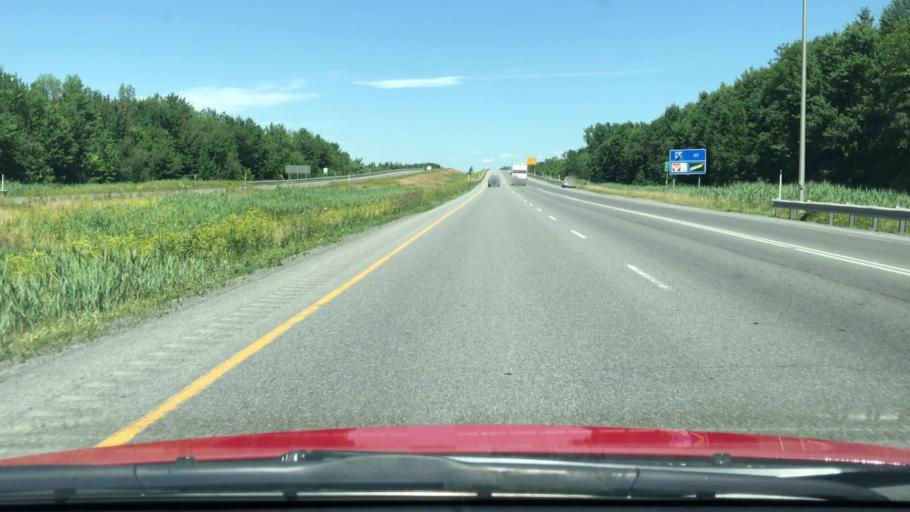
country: CA
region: Quebec
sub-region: Monteregie
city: Saint-Constant
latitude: 45.3811
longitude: -73.6130
